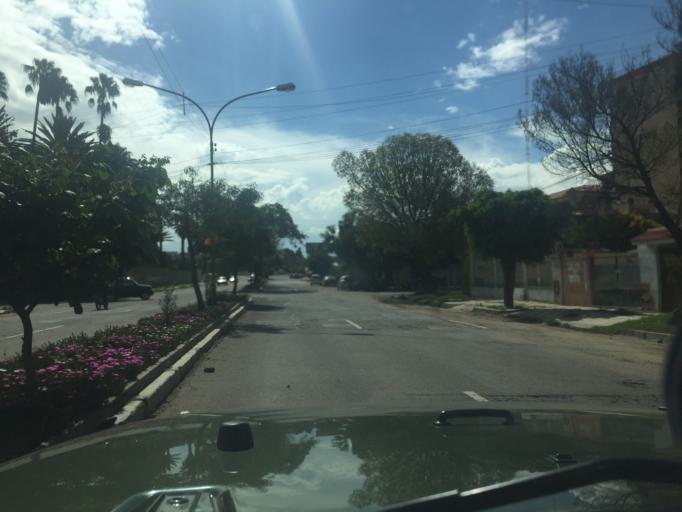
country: BO
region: Cochabamba
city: Cochabamba
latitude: -17.3767
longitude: -66.1706
